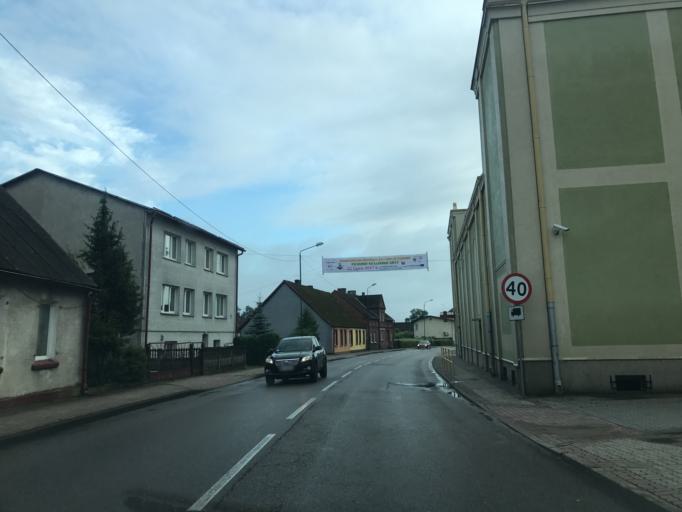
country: PL
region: West Pomeranian Voivodeship
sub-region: Powiat bialogardzki
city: Tychowo
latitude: 53.9284
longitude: 16.2585
